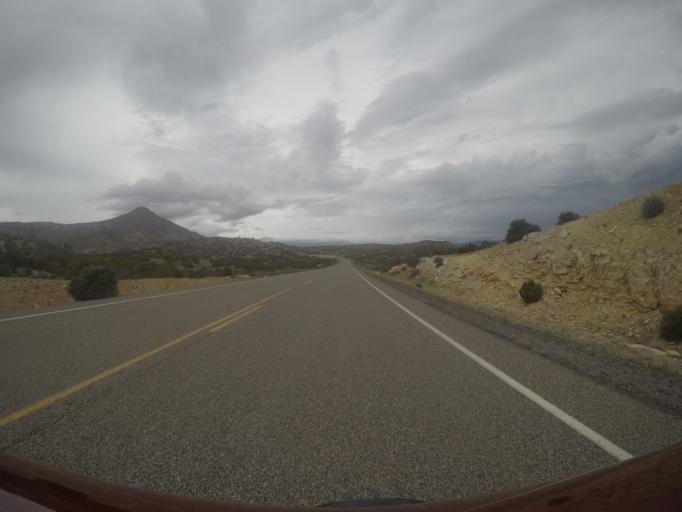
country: US
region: Wyoming
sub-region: Big Horn County
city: Lovell
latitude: 45.0113
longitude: -108.2689
